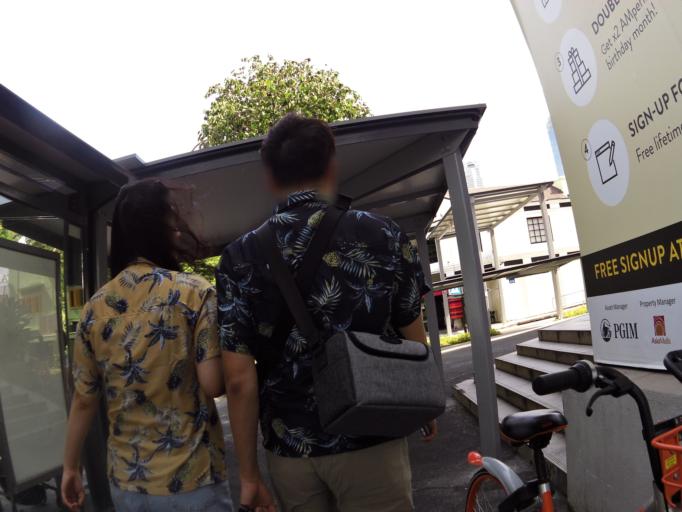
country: SG
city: Singapore
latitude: 1.2917
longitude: 103.8453
